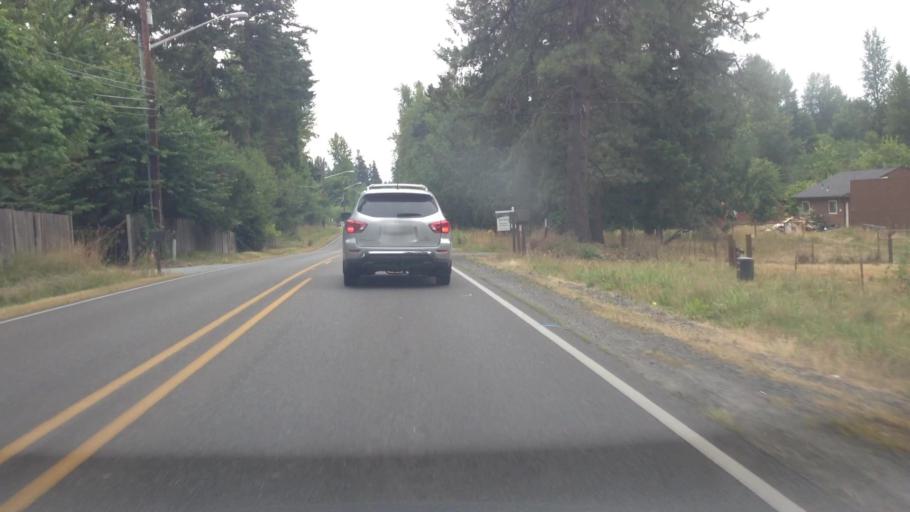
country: US
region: Washington
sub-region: Pierce County
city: South Hill
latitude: 47.1292
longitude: -122.3040
